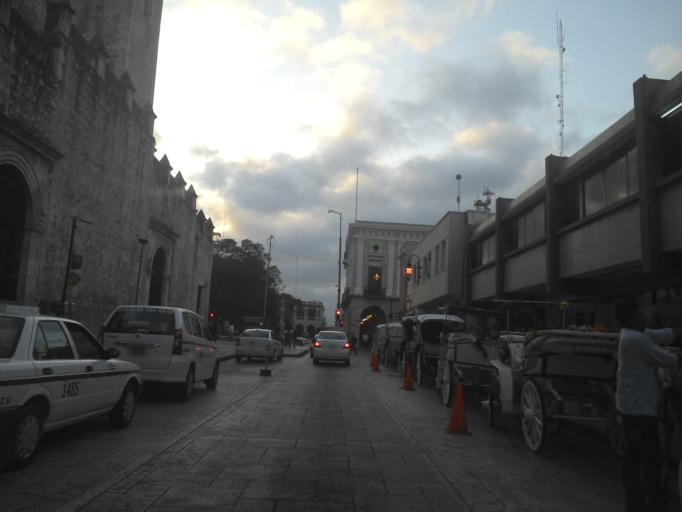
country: MX
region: Yucatan
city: Merida
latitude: 20.9675
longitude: -89.6225
